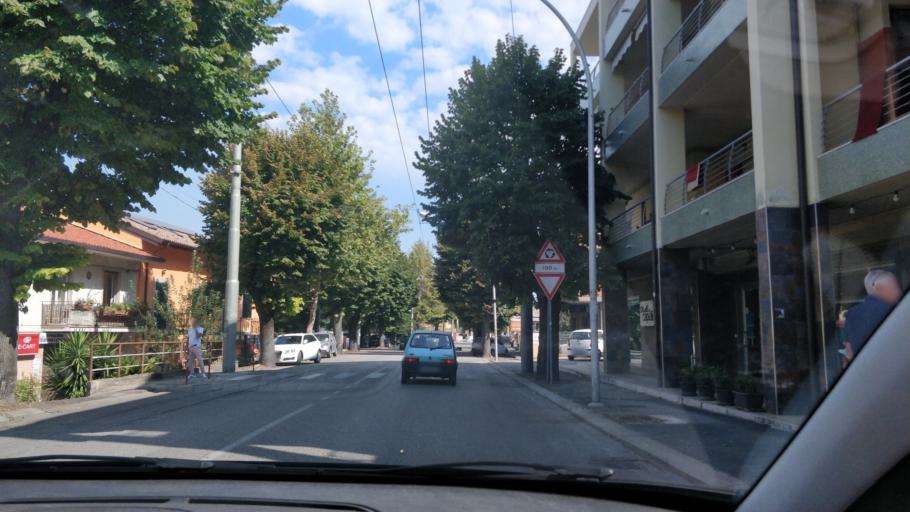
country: IT
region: Abruzzo
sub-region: Provincia di Chieti
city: Chieti
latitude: 42.3739
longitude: 14.1440
